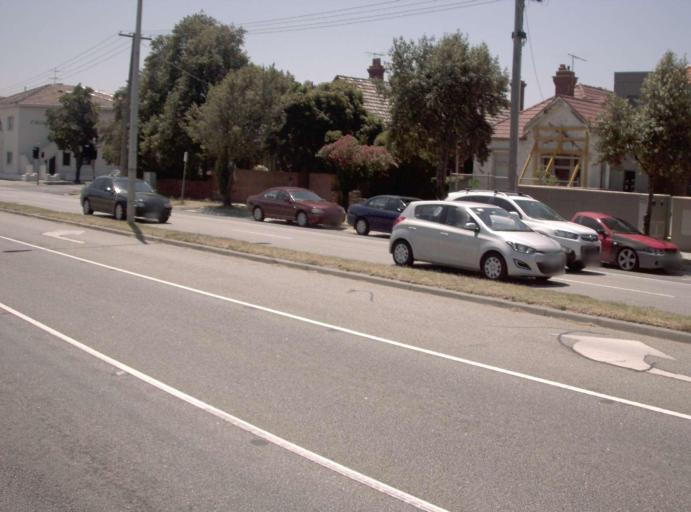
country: AU
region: Victoria
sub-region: Port Phillip
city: Elwood
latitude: -37.8759
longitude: 144.9768
